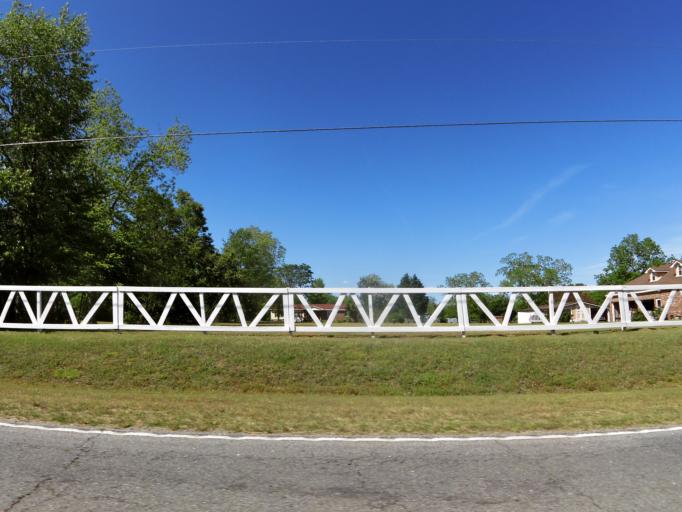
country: US
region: South Carolina
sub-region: Bamberg County
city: Denmark
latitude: 33.3380
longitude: -81.1707
